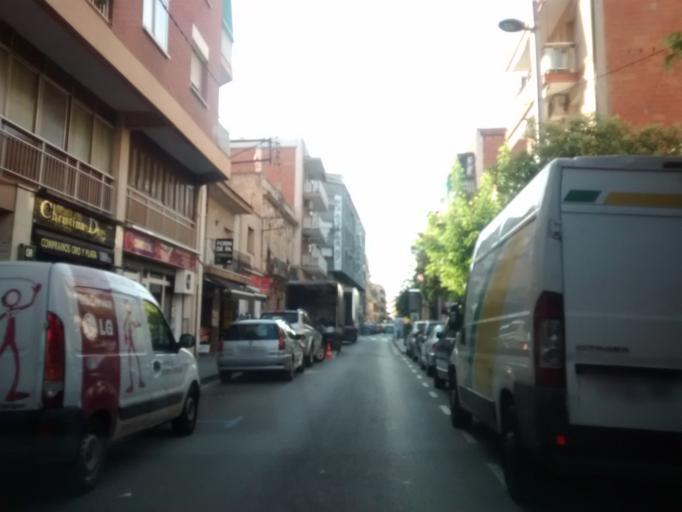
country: ES
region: Catalonia
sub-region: Provincia de Barcelona
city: Sant Vicenc dels Horts
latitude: 41.3985
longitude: 2.0079
